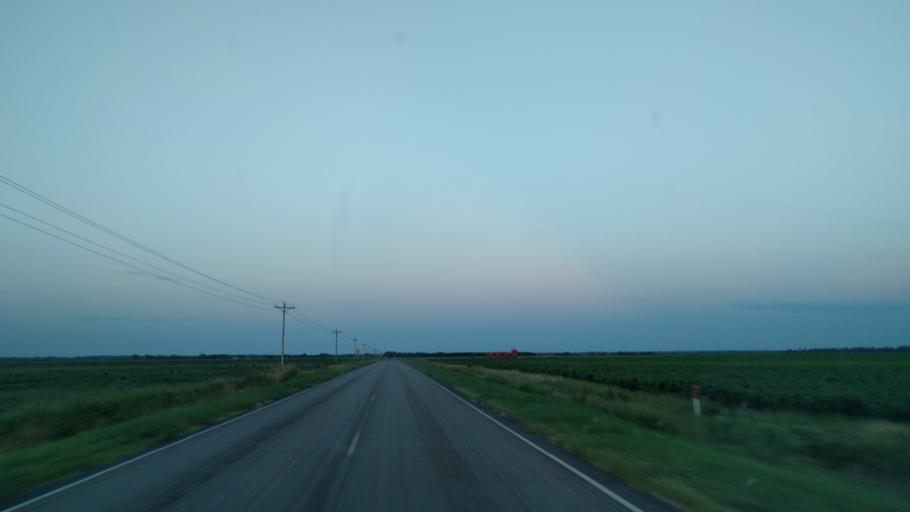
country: US
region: Kansas
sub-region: Reno County
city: Nickerson
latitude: 38.2171
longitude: -98.1014
